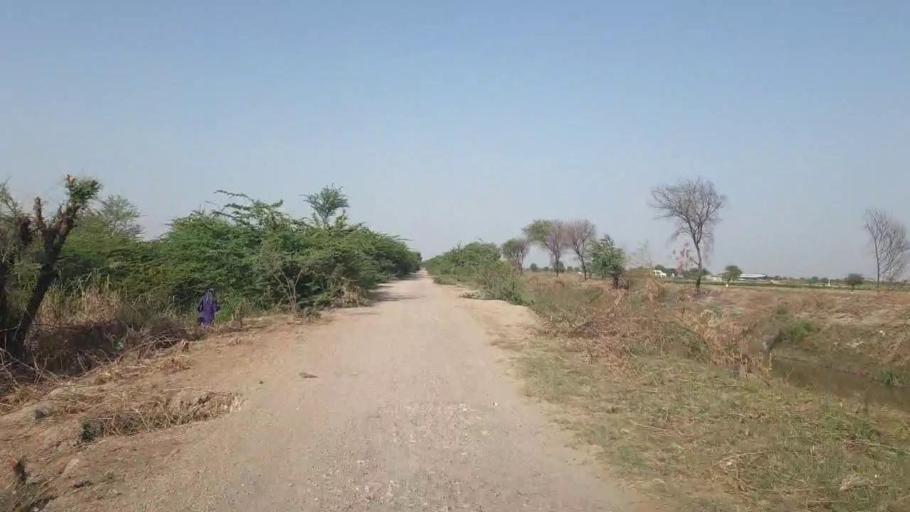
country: PK
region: Sindh
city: Dhoro Naro
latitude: 25.4663
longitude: 69.5386
